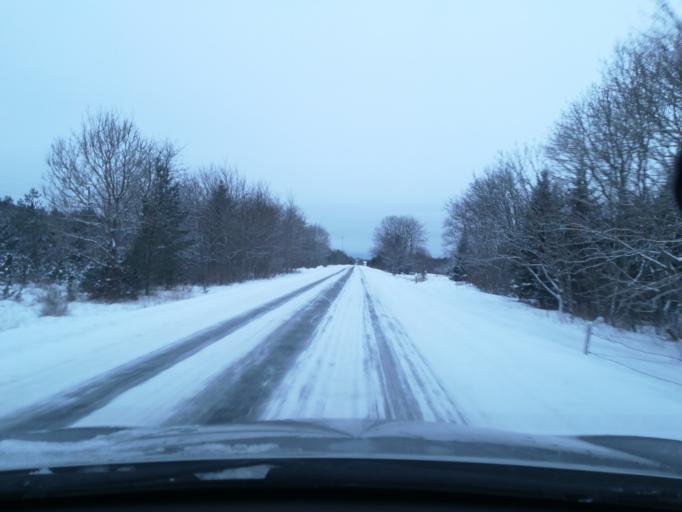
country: EE
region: Harju
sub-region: Keila linn
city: Keila
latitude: 59.3656
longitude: 24.3312
